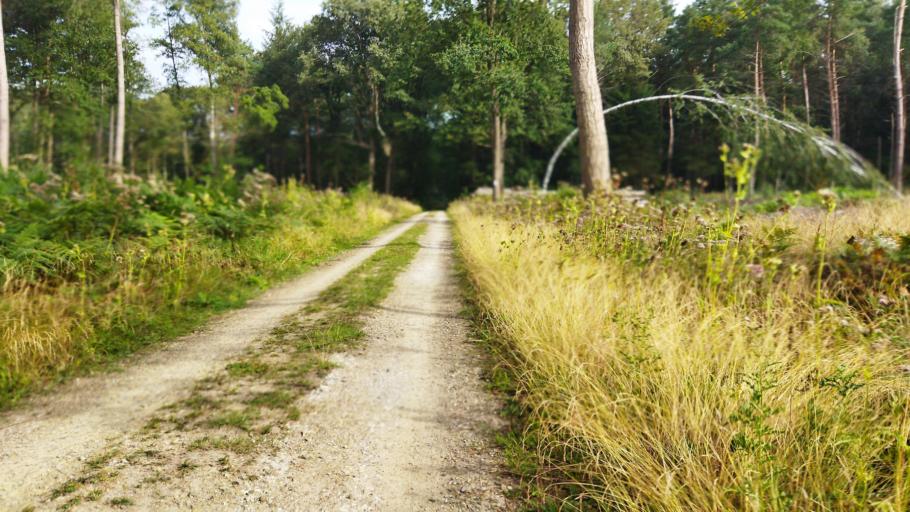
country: DE
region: Lower Saxony
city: Bad Rothenfelde
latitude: 52.0841
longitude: 8.1589
